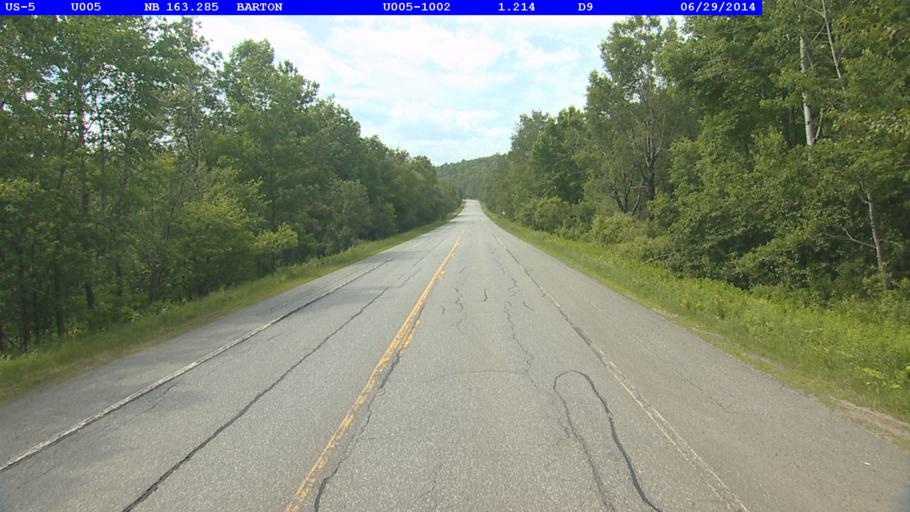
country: US
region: Vermont
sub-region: Caledonia County
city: Lyndonville
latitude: 44.7076
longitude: -72.1172
